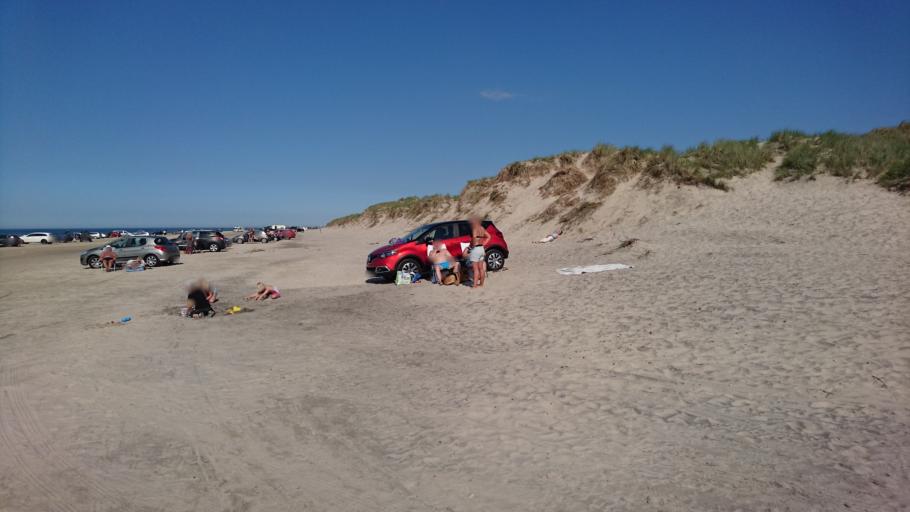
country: DK
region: North Denmark
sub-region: Hjorring Kommune
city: Sindal
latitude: 57.5966
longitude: 10.1816
